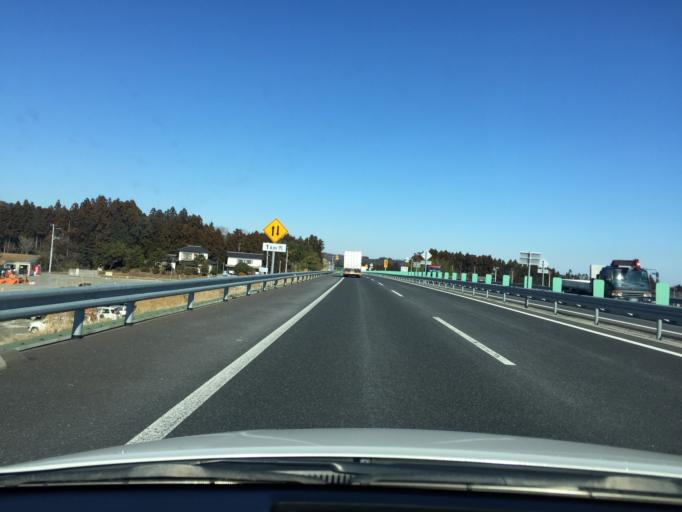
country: JP
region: Miyagi
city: Marumori
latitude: 37.7665
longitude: 140.9014
